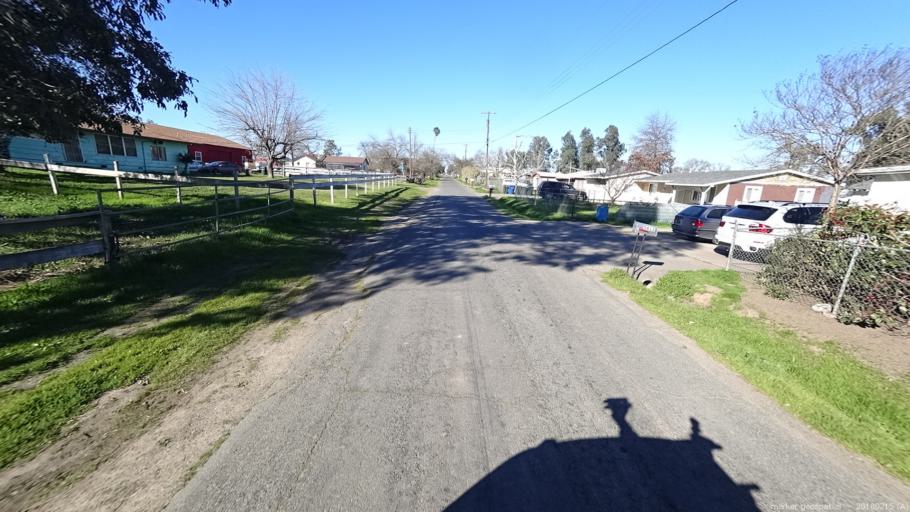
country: US
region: California
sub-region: Sacramento County
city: Rio Linda
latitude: 38.6734
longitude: -121.4615
